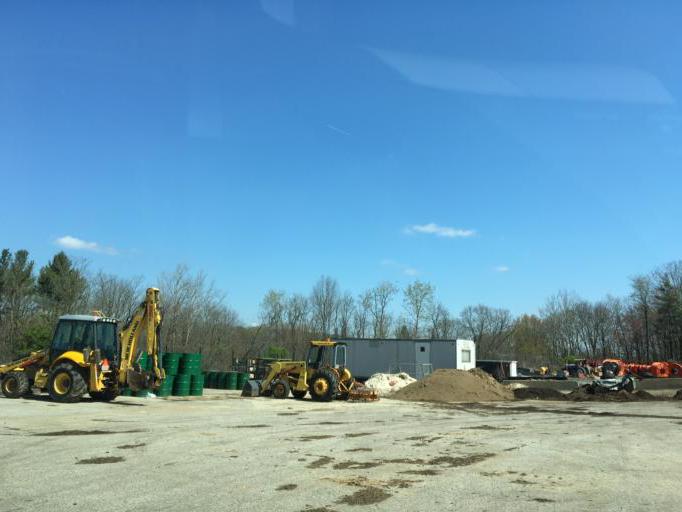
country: US
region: Maryland
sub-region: Baltimore County
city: Cockeysville
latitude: 39.4672
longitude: -76.6245
